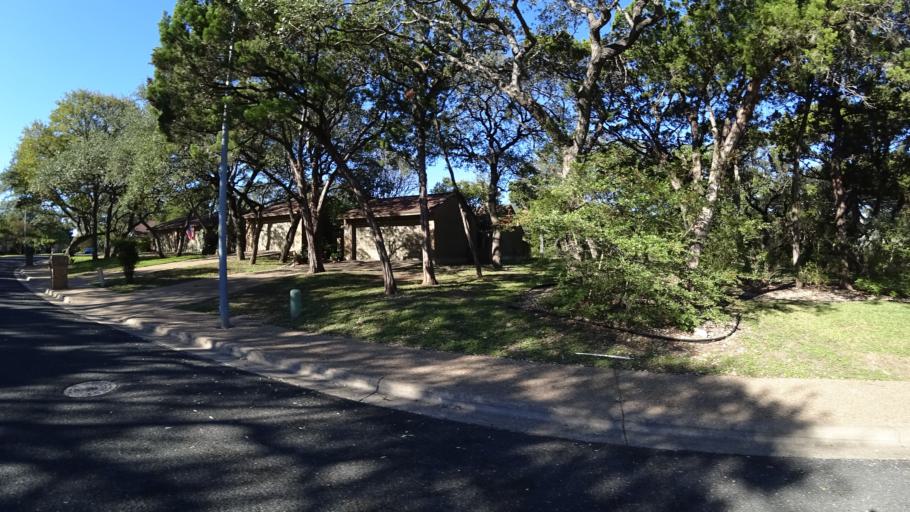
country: US
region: Texas
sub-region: Travis County
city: West Lake Hills
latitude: 30.3556
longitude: -97.7921
